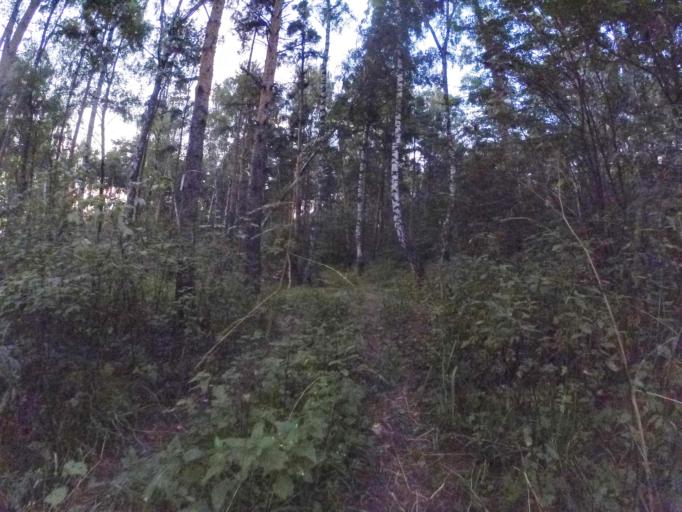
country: RU
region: Moscow
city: Kapotnya
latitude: 55.6610
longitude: 37.8126
